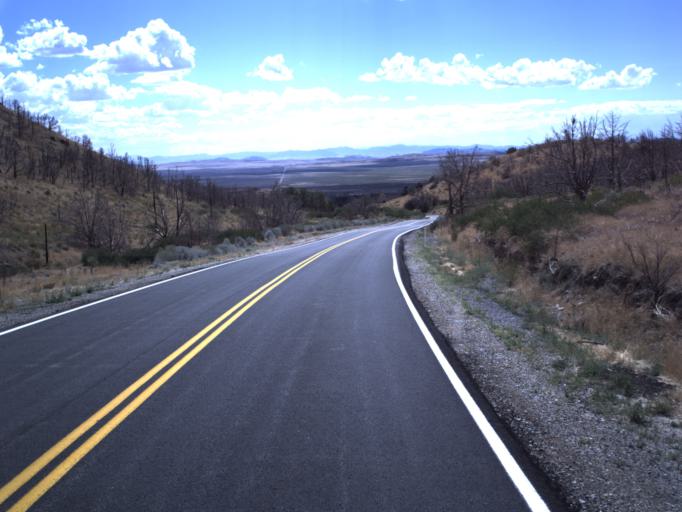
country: US
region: Utah
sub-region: Tooele County
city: Grantsville
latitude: 40.3428
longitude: -112.6051
